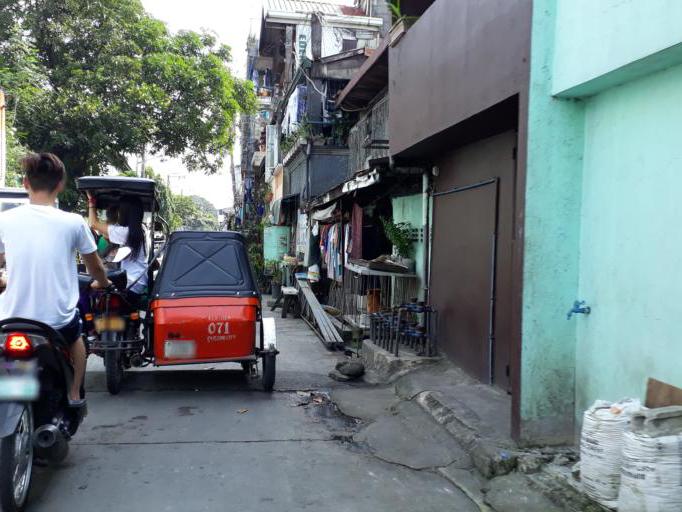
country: PH
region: Calabarzon
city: Bagong Pagasa
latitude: 14.6710
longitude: 121.0008
